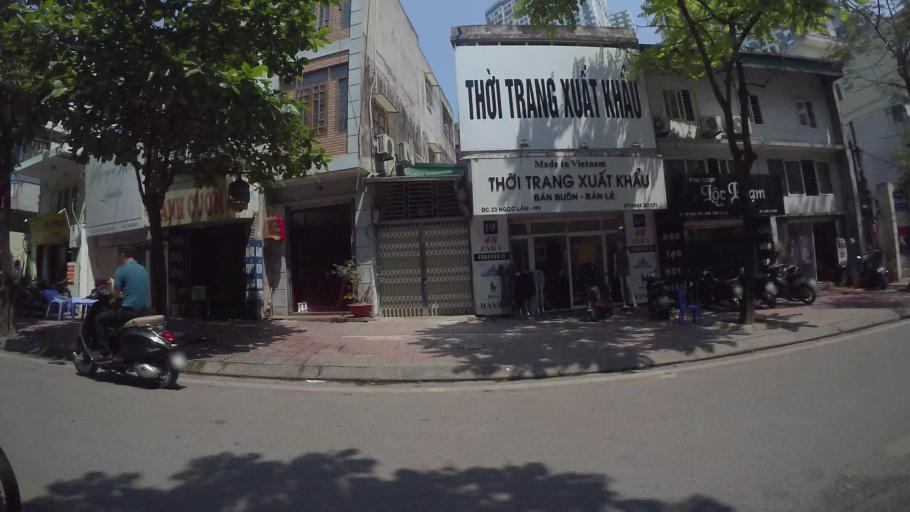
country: VN
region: Ha Noi
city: Hoan Kiem
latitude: 21.0440
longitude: 105.8665
